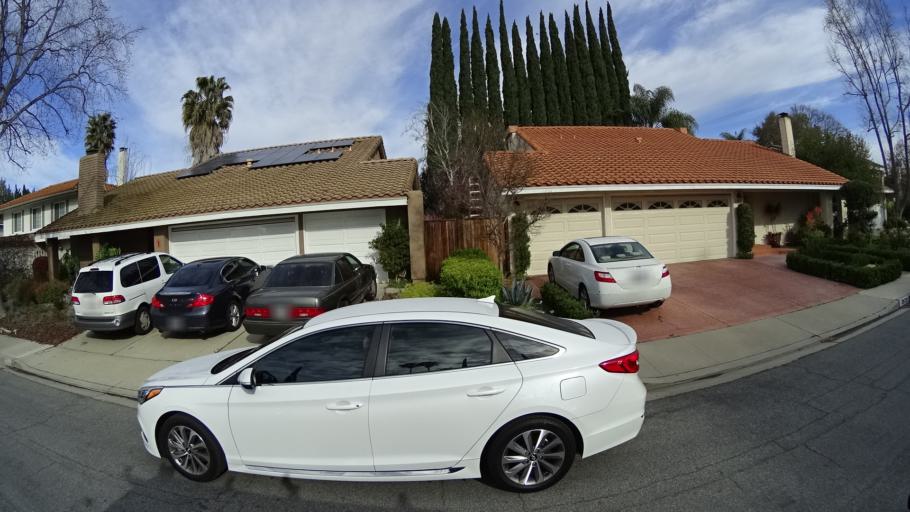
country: US
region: California
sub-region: Ventura County
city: Thousand Oaks
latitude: 34.1534
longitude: -118.8402
